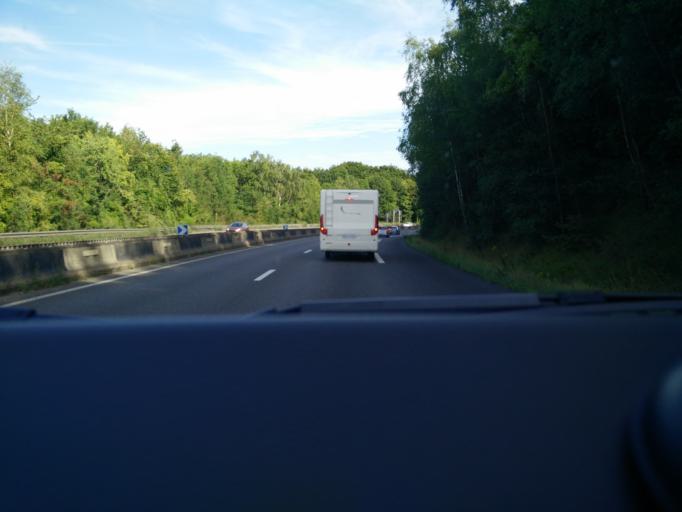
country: FR
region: Lorraine
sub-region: Departement de Meurthe-et-Moselle
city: Vandoeuvre-les-Nancy
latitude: 48.6415
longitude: 6.1680
